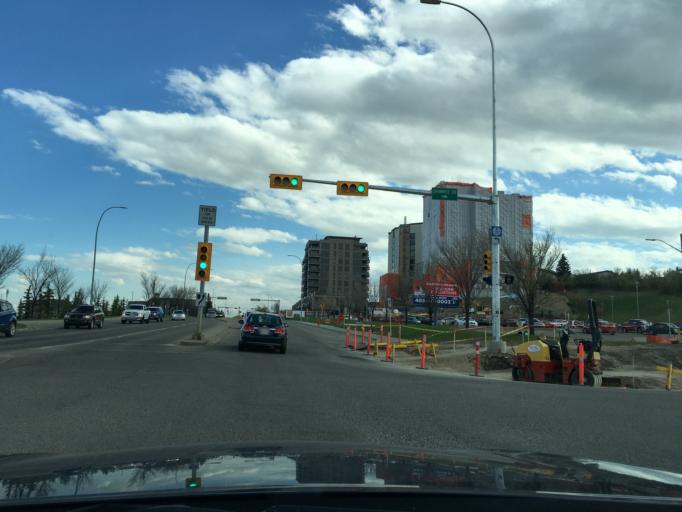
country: CA
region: Alberta
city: Calgary
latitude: 50.9242
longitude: -114.0751
